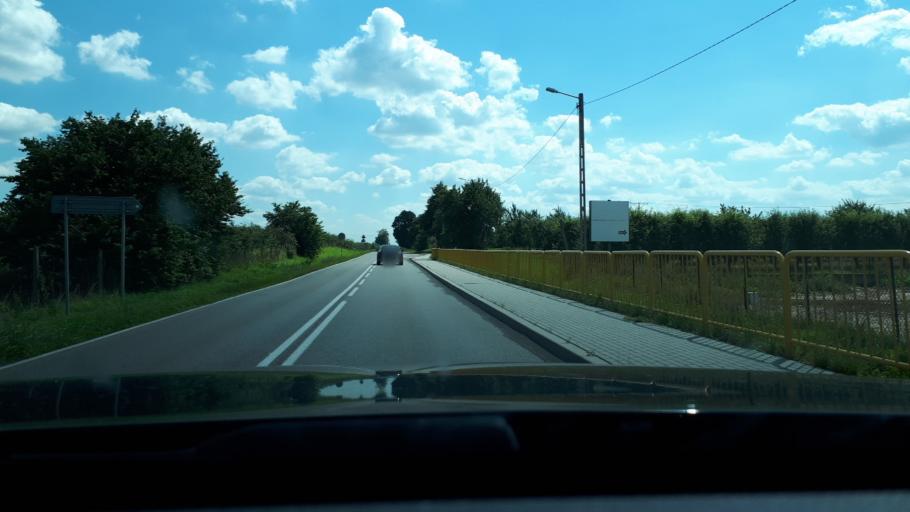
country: PL
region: Masovian Voivodeship
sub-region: Powiat grojecki
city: Warka
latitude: 51.8223
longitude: 21.1937
